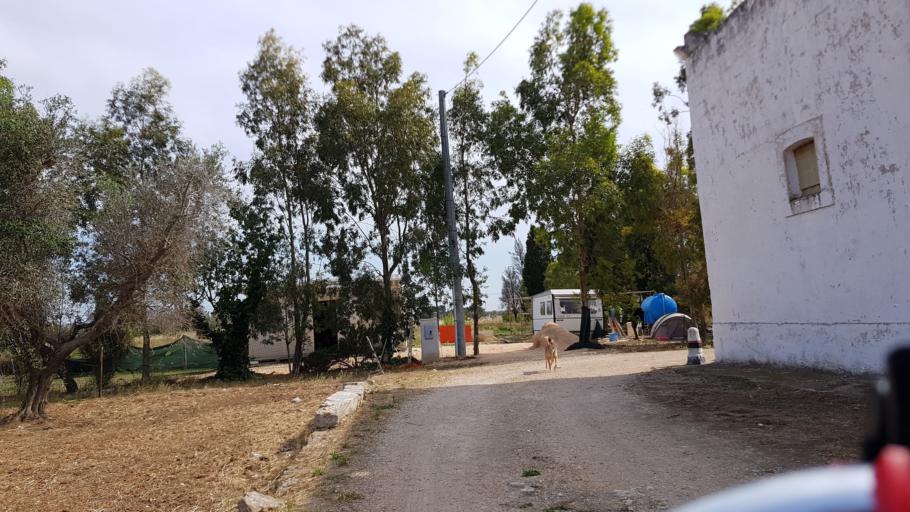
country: IT
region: Apulia
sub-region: Provincia di Brindisi
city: San Vito dei Normanni
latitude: 40.6536
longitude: 17.8000
